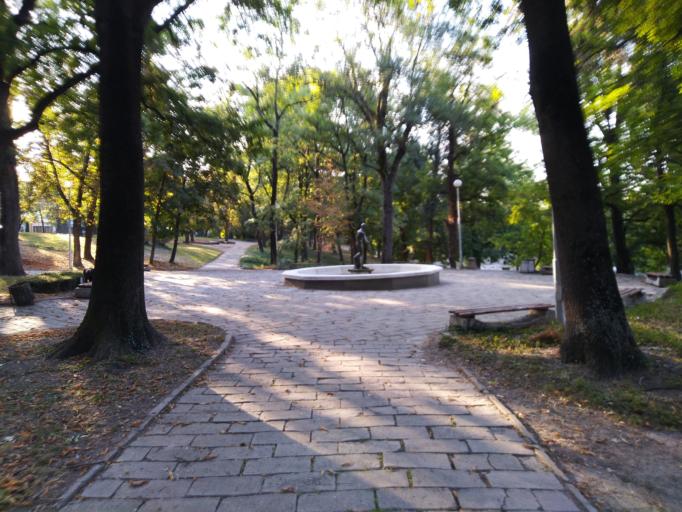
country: BG
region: Plovdiv
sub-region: Obshtina Khisarya
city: Khisarya
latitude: 42.5014
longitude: 24.7033
